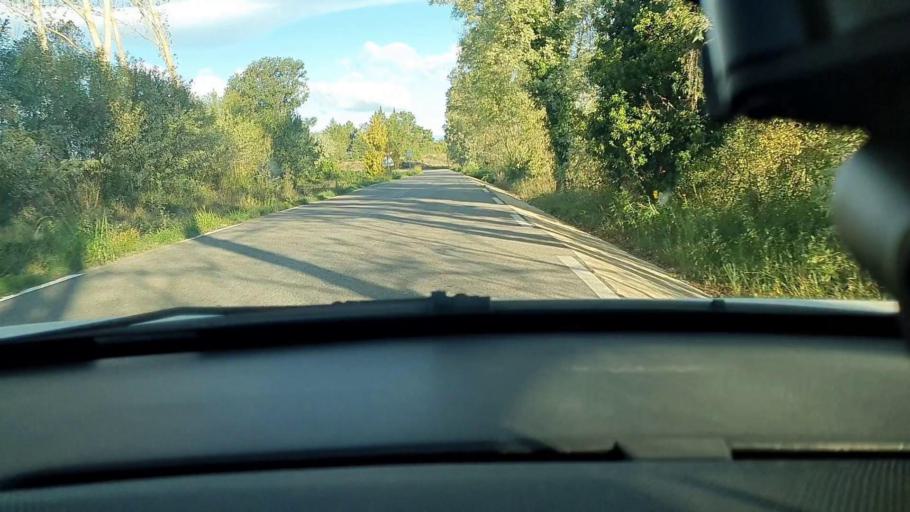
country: FR
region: Languedoc-Roussillon
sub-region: Departement du Gard
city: Saint-Ambroix
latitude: 44.2361
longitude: 4.2712
